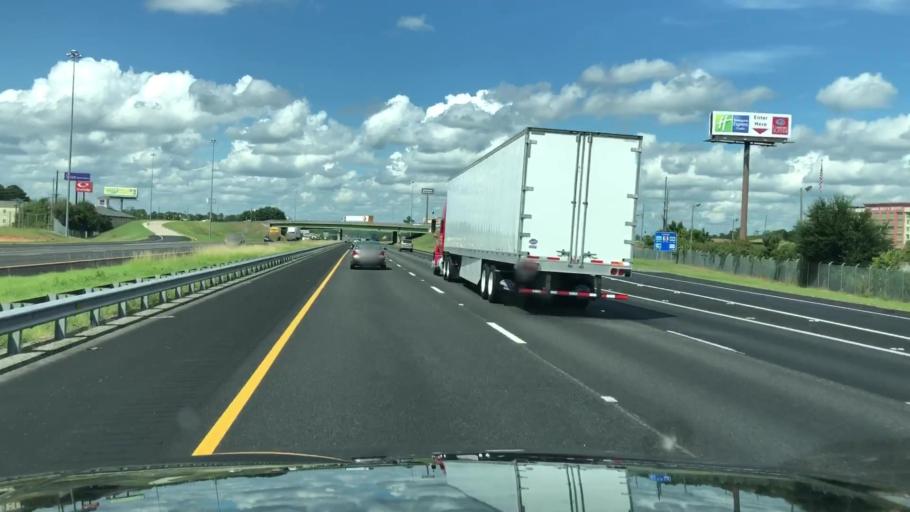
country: US
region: Georgia
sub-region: Lowndes County
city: Remerton
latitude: 30.8422
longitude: -83.3290
